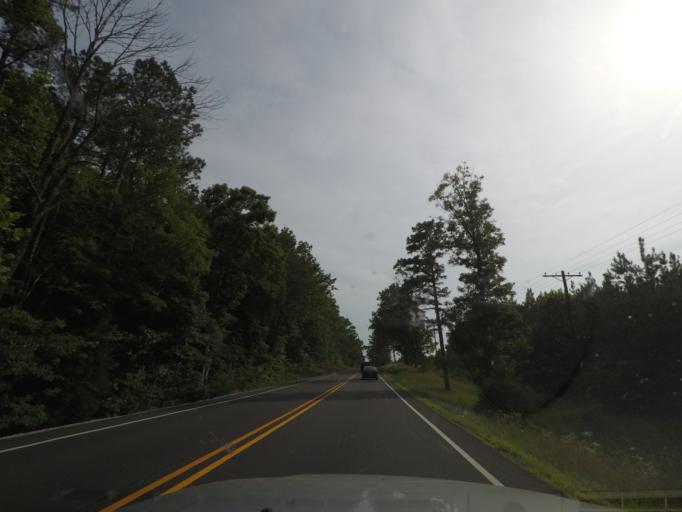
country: US
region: Virginia
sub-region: Prince Edward County
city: Hampden Sydney
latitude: 37.1153
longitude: -78.4621
